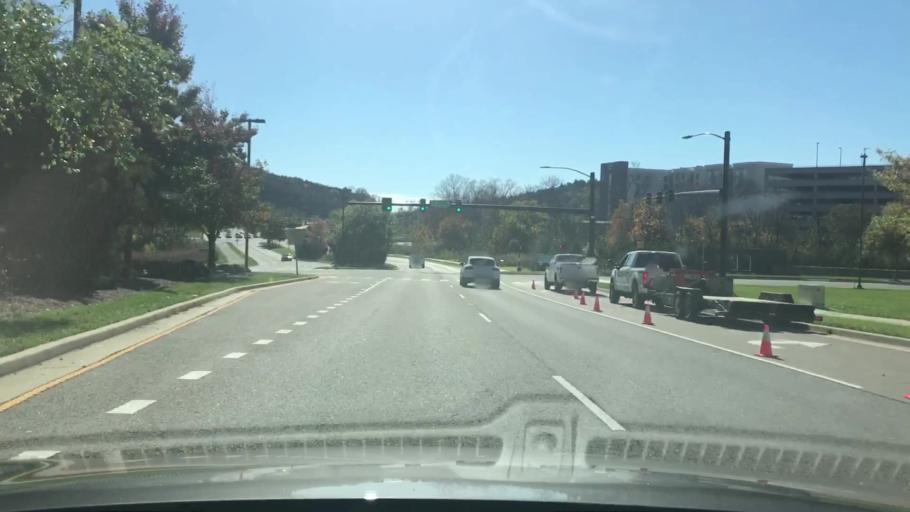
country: US
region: Tennessee
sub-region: Williamson County
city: Franklin
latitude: 35.9359
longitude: -86.8108
